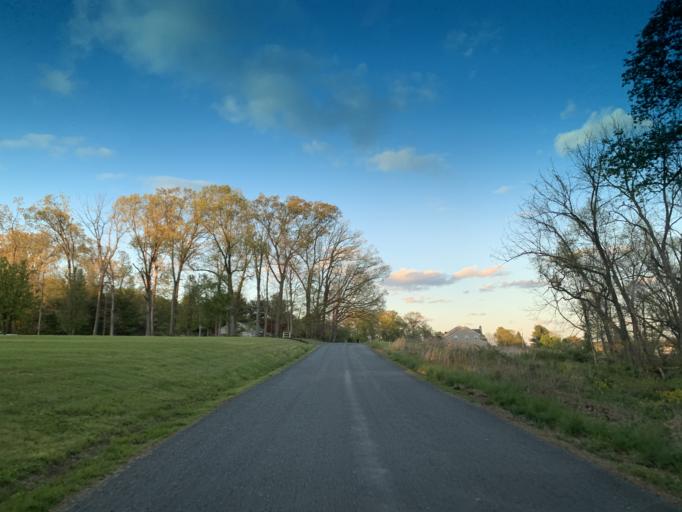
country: US
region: Maryland
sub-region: Harford County
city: Jarrettsville
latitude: 39.6575
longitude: -76.4212
